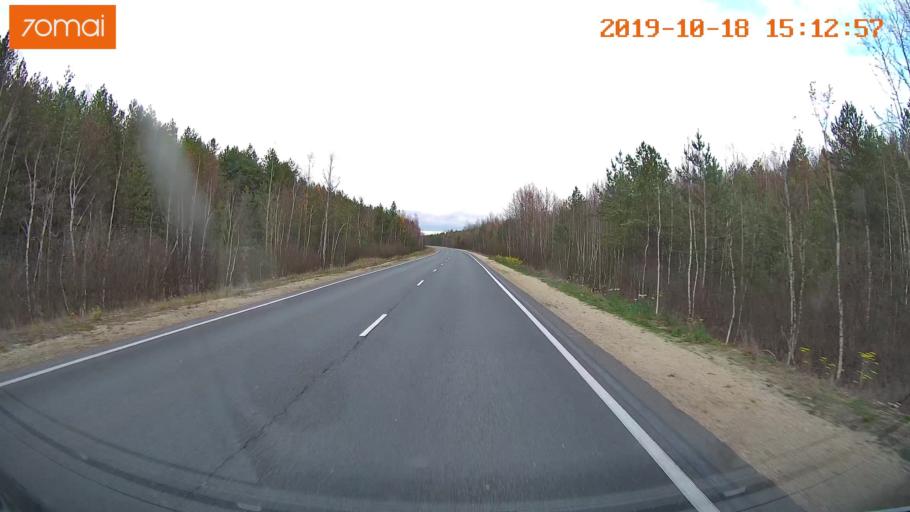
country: RU
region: Vladimir
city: Gus'-Khrustal'nyy
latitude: 55.5805
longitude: 40.7096
